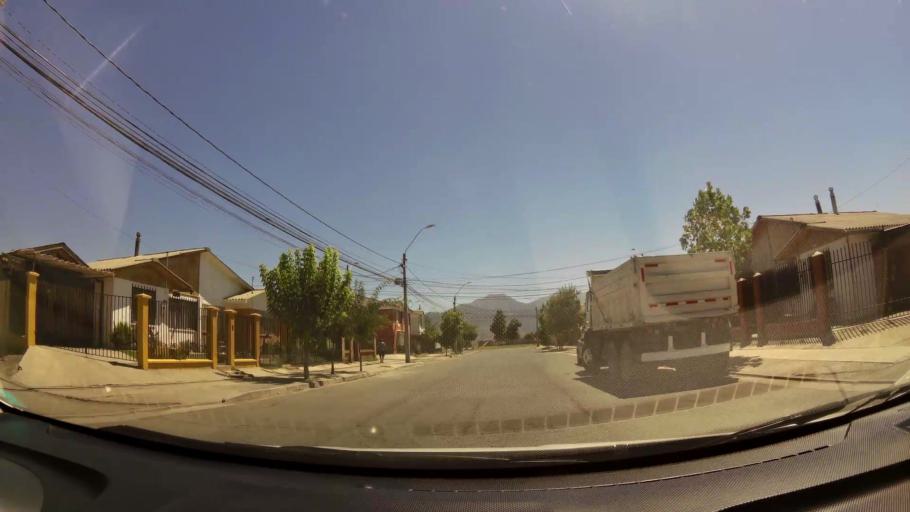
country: CL
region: O'Higgins
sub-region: Provincia de Cachapoal
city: Rancagua
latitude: -34.1667
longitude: -70.7813
